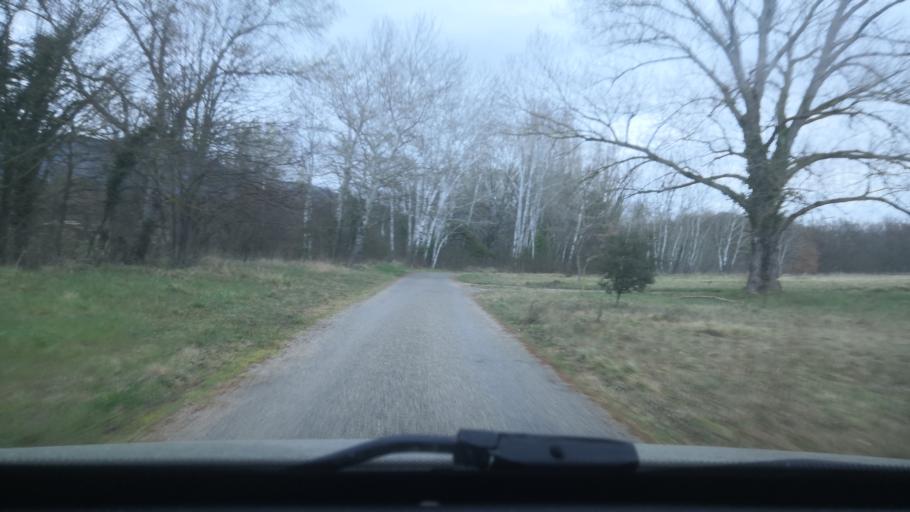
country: FR
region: Rhone-Alpes
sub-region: Departement de la Drome
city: Dieulefit
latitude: 44.5282
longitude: 5.0140
